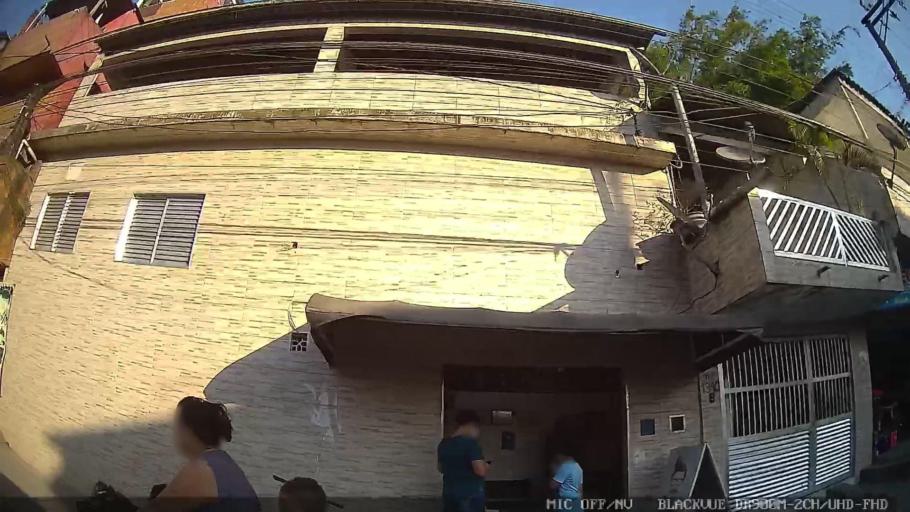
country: BR
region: Sao Paulo
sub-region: Guaruja
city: Guaruja
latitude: -23.9766
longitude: -46.2578
